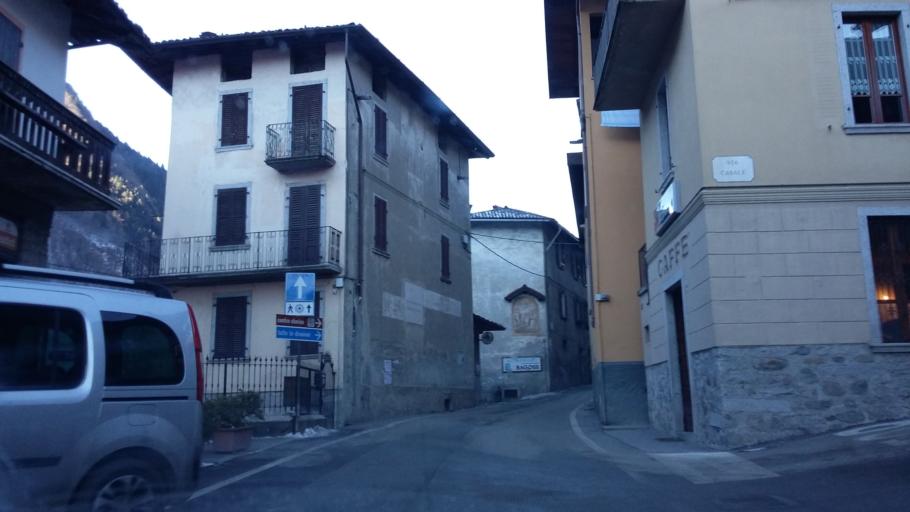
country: IT
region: Lombardy
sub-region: Provincia di Brescia
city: Bagolino
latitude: 45.8208
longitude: 10.4668
